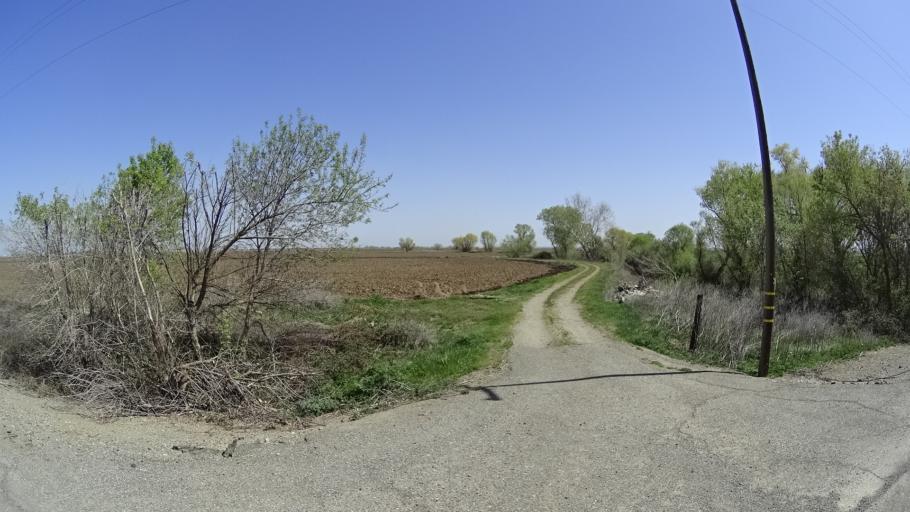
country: US
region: California
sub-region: Glenn County
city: Willows
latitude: 39.5052
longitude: -122.1367
